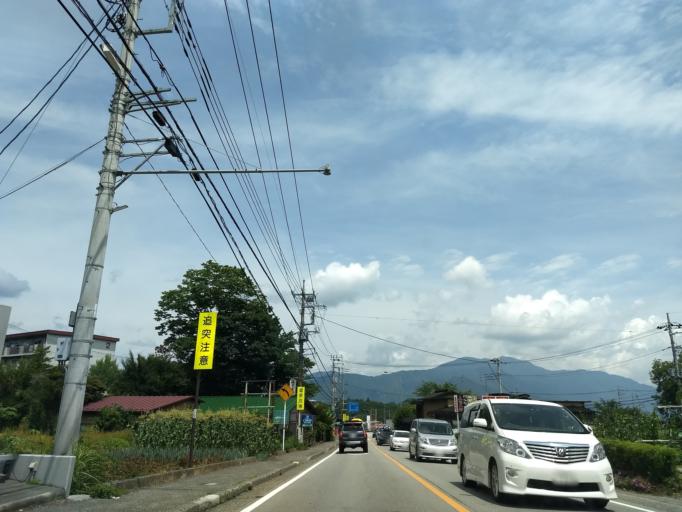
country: JP
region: Yamanashi
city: Fujikawaguchiko
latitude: 35.4613
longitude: 138.8041
